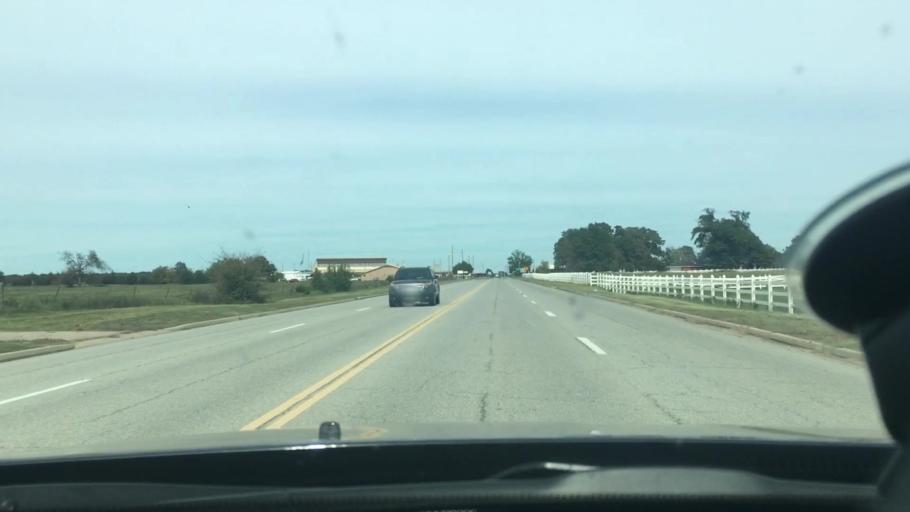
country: US
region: Oklahoma
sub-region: Atoka County
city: Atoka
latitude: 34.3893
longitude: -96.1455
